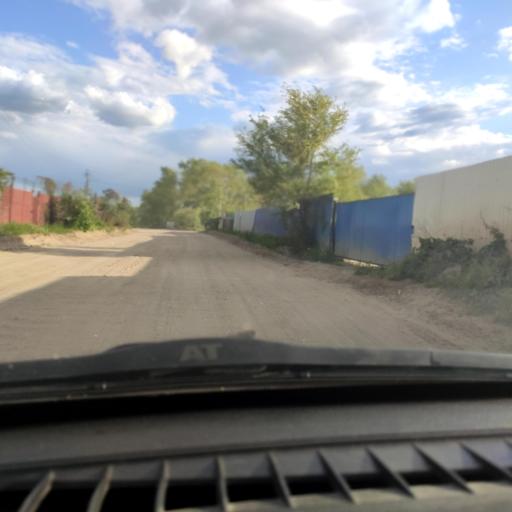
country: RU
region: Samara
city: Zhigulevsk
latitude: 53.4536
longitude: 49.5350
